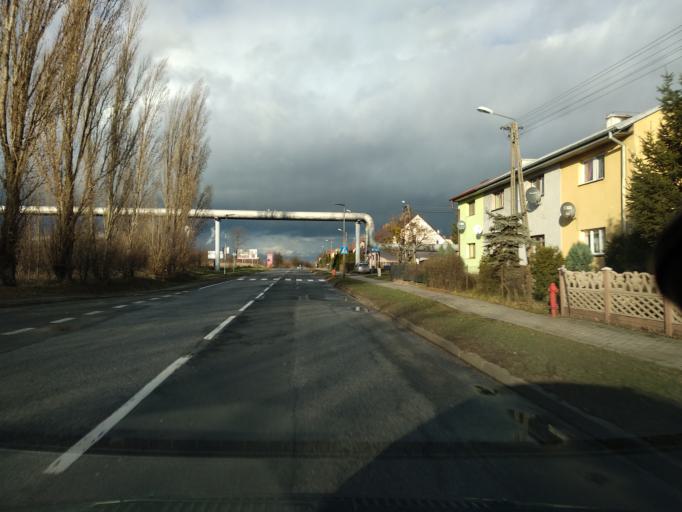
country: PL
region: Greater Poland Voivodeship
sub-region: Konin
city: Konin
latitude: 52.2670
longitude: 18.2672
